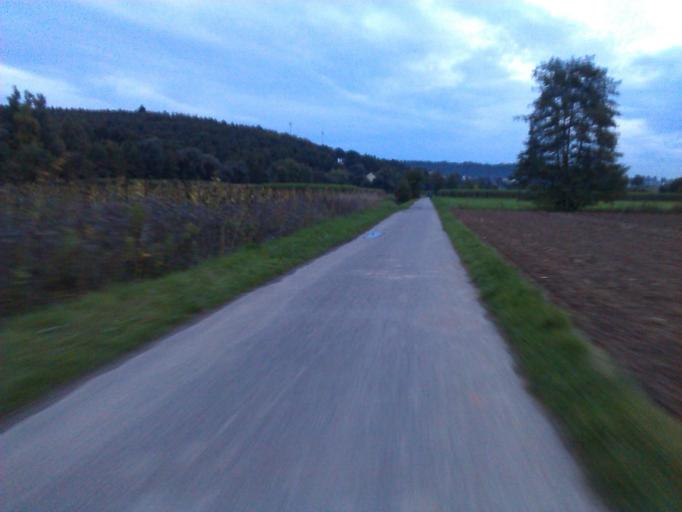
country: DE
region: Baden-Wuerttemberg
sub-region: Karlsruhe Region
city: Zuzenhausen
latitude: 49.2813
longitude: 8.8289
